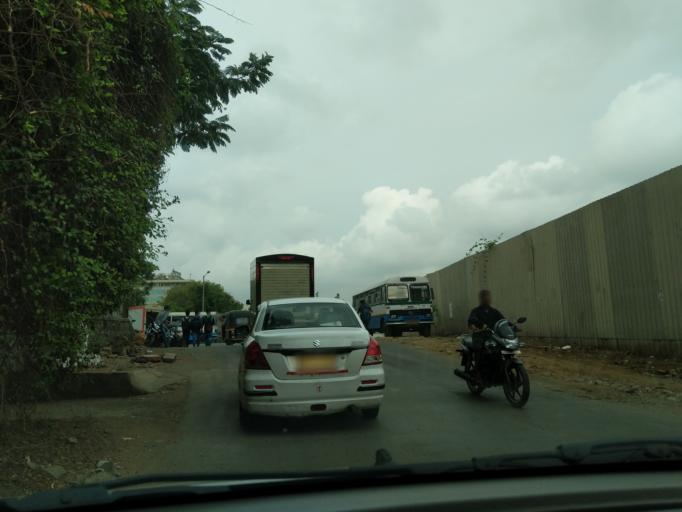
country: IN
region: Maharashtra
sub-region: Mumbai Suburban
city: Mumbai
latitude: 19.1004
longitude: 72.8782
